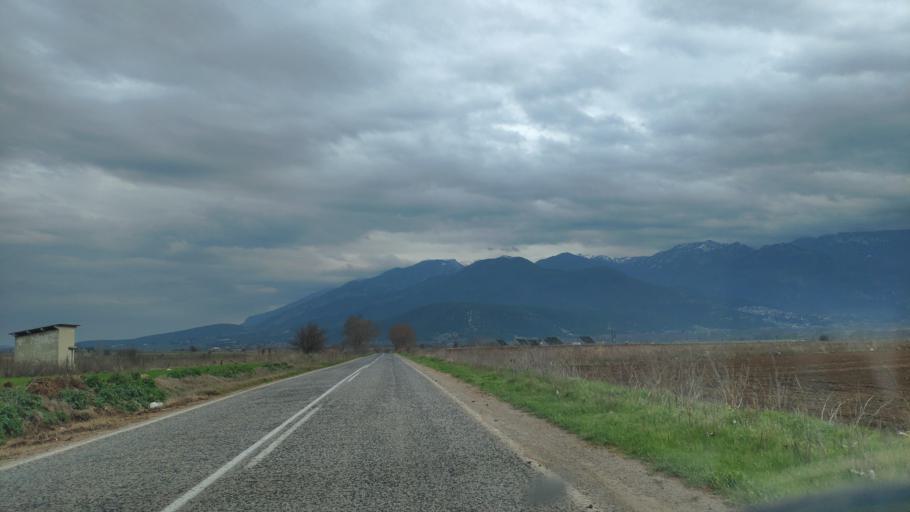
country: GR
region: Central Greece
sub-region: Nomos Fthiotidos
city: Amfikleia
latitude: 38.6921
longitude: 22.5286
